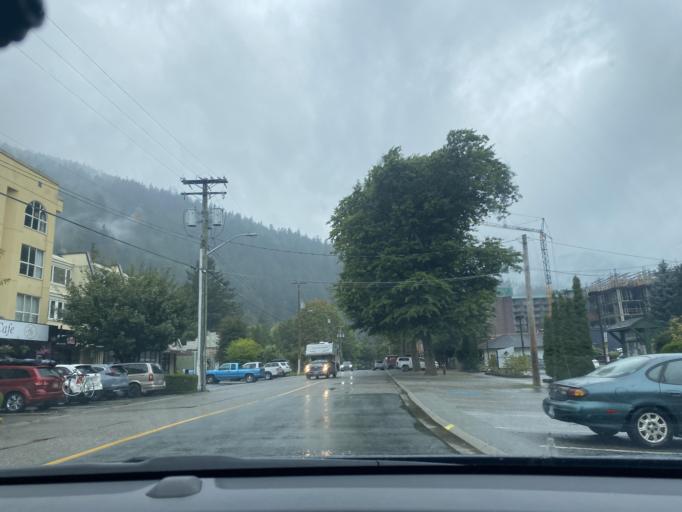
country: CA
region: British Columbia
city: Agassiz
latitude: 49.3025
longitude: -121.7859
